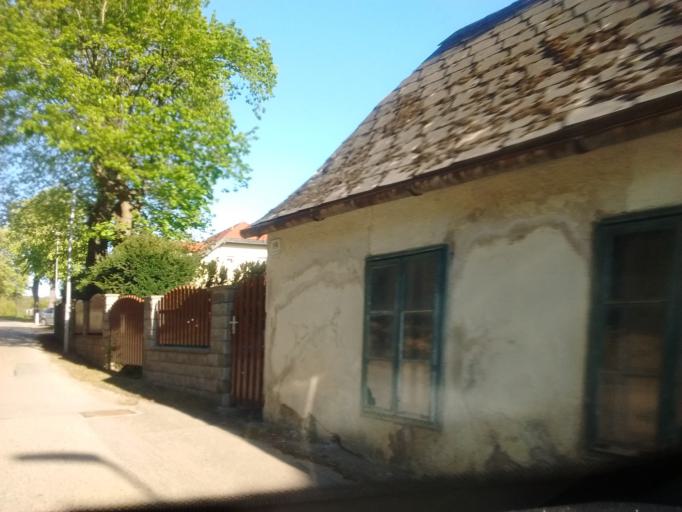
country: AT
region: Lower Austria
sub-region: Politischer Bezirk Modling
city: Gaaden
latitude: 48.0744
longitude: 16.1919
